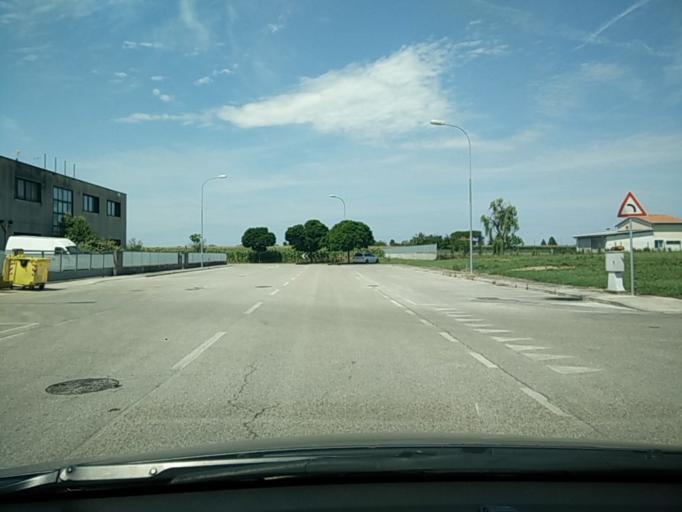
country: IT
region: Veneto
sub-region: Provincia di Venezia
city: Iesolo
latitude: 45.5534
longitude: 12.6548
